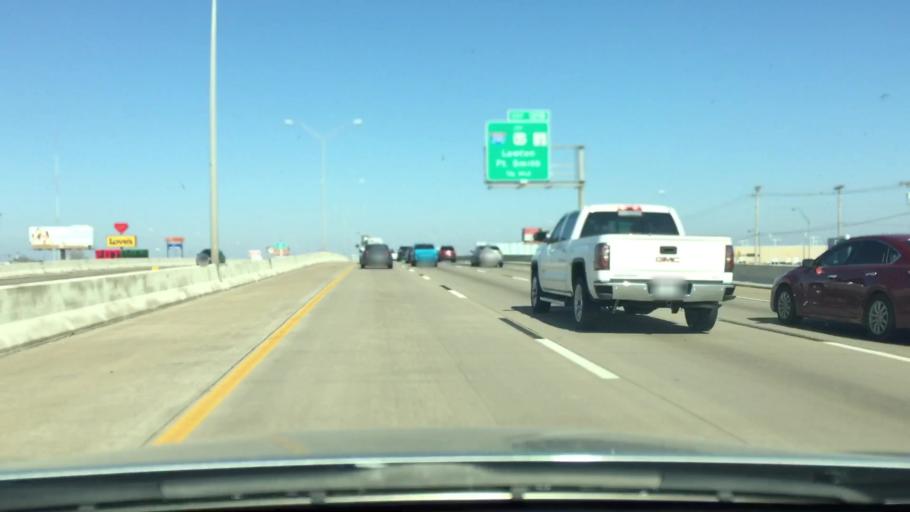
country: US
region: Oklahoma
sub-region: Cleveland County
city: Moore
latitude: 35.3763
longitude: -97.4949
